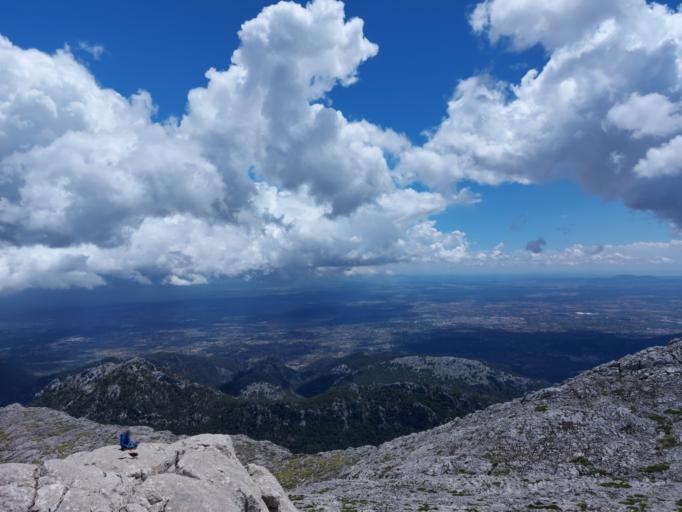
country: ES
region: Balearic Islands
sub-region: Illes Balears
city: Escorca
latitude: 39.8060
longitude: 2.8530
